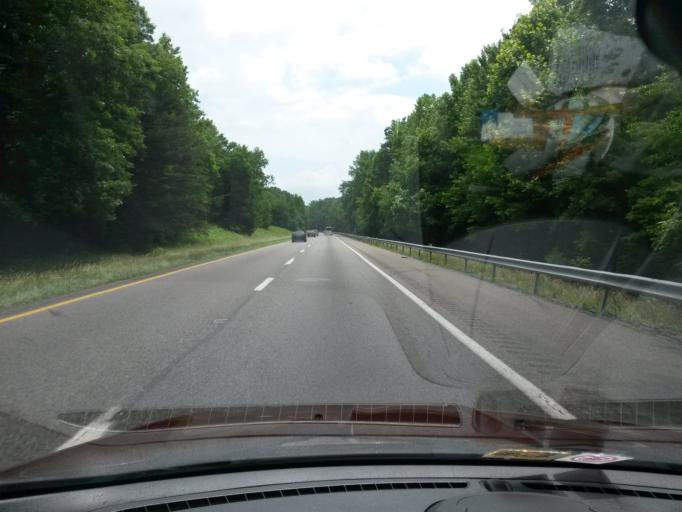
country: US
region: Virginia
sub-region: Goochland County
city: Goochland
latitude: 37.7283
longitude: -77.8233
